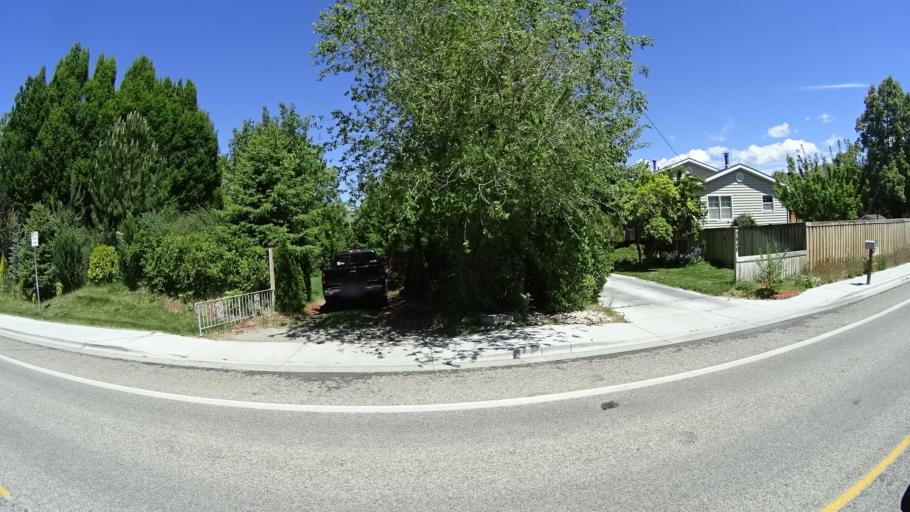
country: US
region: Idaho
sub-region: Ada County
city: Boise
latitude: 43.5641
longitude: -116.1387
